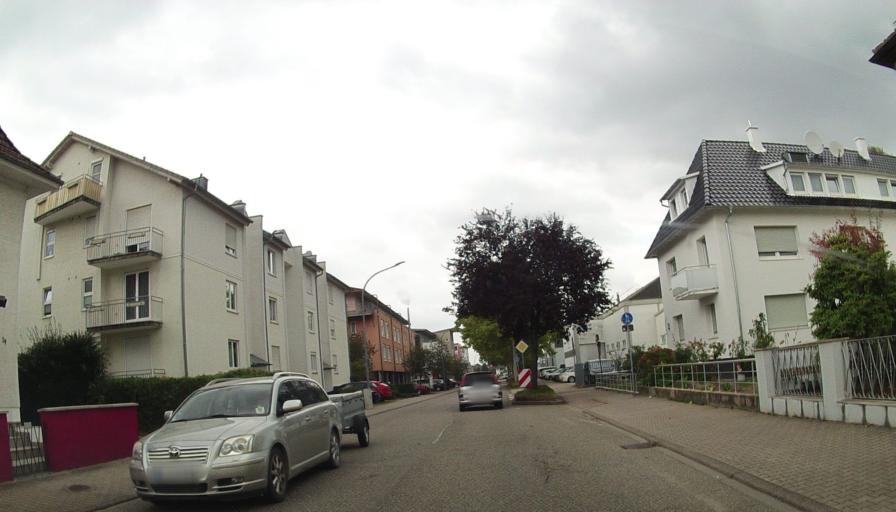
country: DE
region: Baden-Wuerttemberg
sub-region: Karlsruhe Region
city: Gaggenau
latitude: 48.8077
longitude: 8.3205
